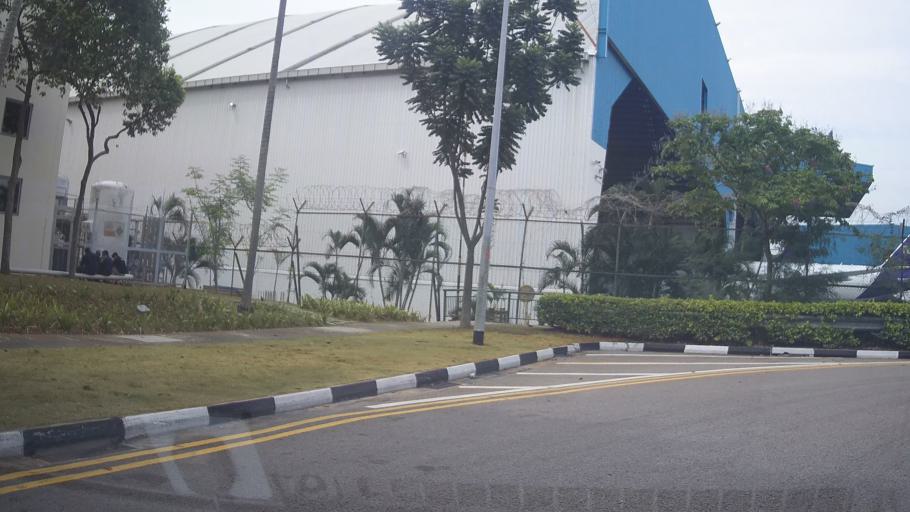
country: SG
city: Singapore
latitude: 1.3489
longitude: 103.9723
